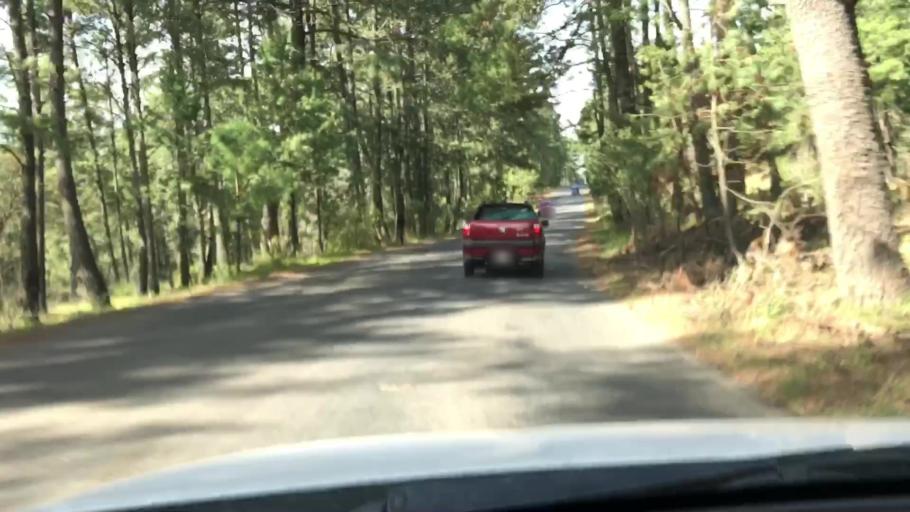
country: MX
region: Jalisco
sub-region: Amacueca
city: Tepec
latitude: 20.0539
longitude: -103.6986
